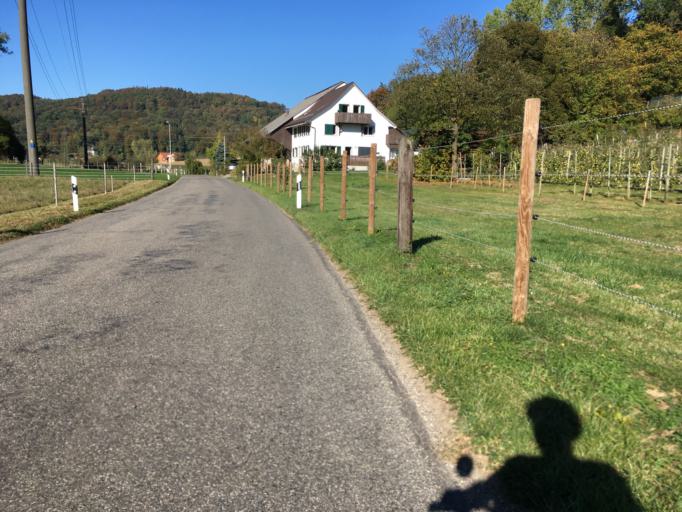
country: CH
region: Zurich
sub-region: Bezirk Buelach
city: Buelach / Soligaenter
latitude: 47.5421
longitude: 8.5423
